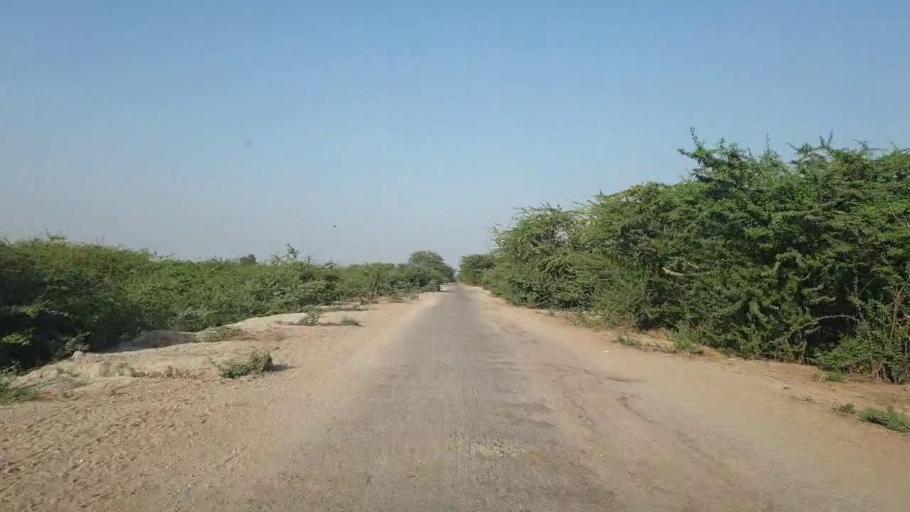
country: PK
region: Sindh
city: Chor
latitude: 25.5511
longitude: 69.7884
